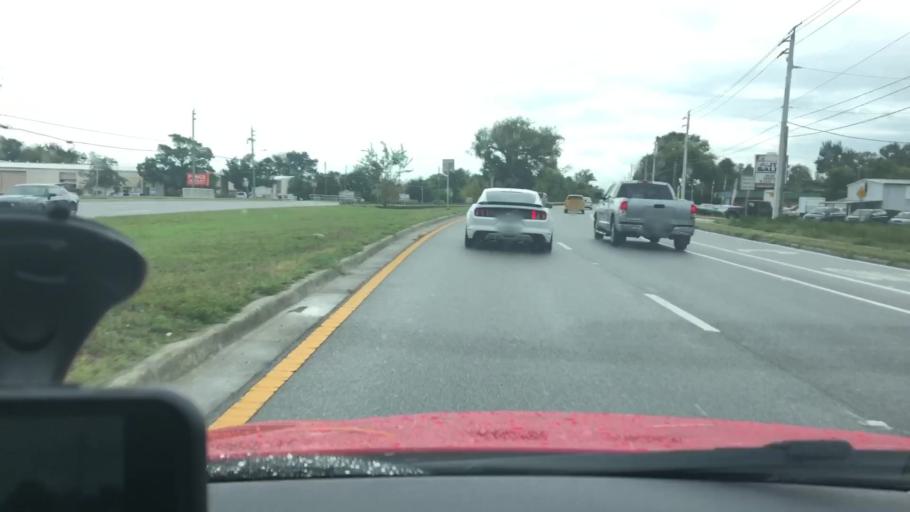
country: US
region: Florida
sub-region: Volusia County
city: South Daytona
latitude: 29.1730
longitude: -81.0275
